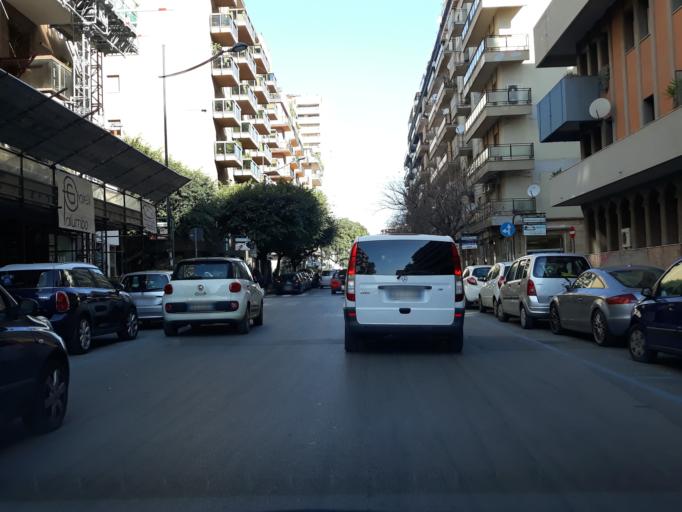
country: IT
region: Sicily
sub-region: Palermo
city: Palermo
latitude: 38.1353
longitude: 13.3451
